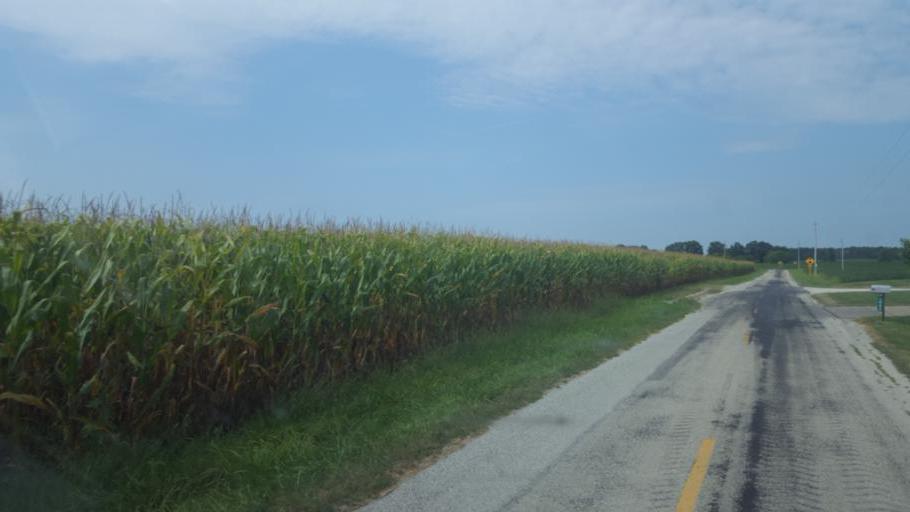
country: US
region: Ohio
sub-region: Delaware County
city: Ashley
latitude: 40.4916
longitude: -83.0023
